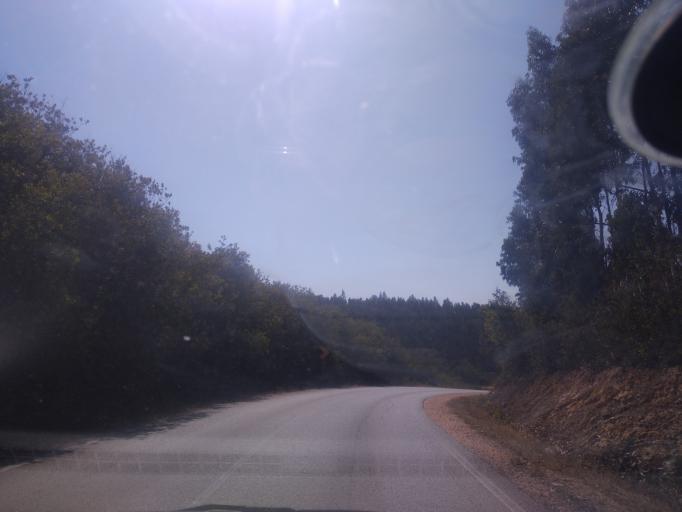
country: PT
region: Faro
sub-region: Aljezur
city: Aljezur
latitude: 37.2204
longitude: -8.8004
